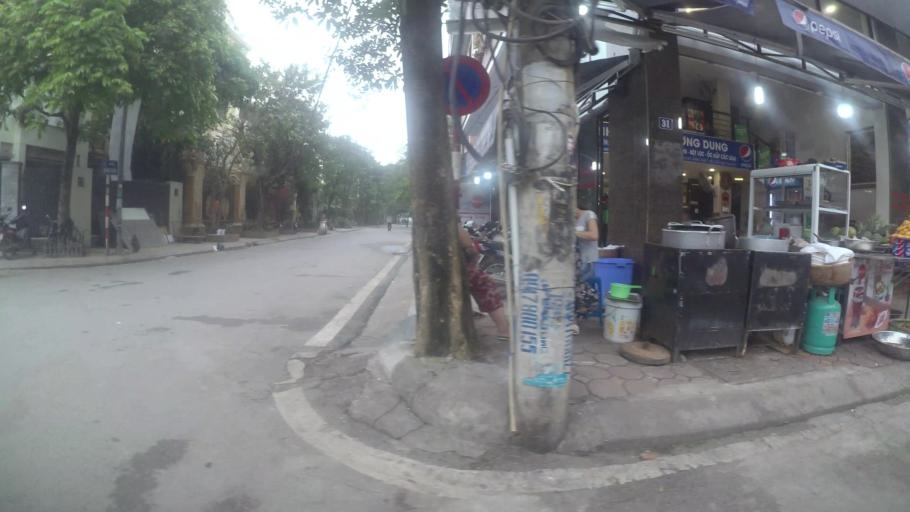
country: VN
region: Ha Noi
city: Tay Ho
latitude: 21.0568
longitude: 105.8204
